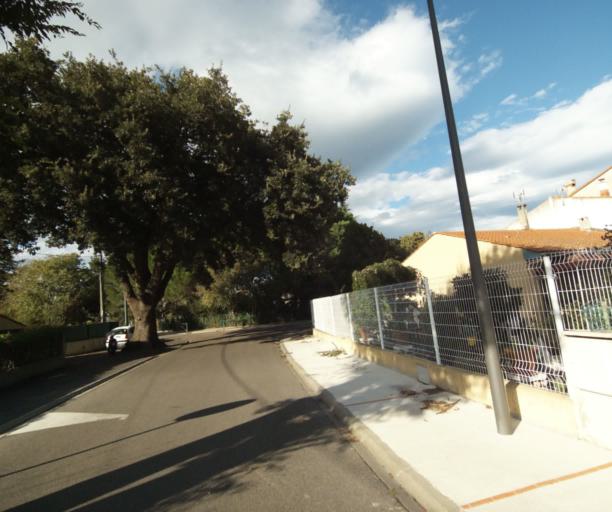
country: FR
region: Languedoc-Roussillon
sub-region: Departement des Pyrenees-Orientales
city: Argelers
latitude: 42.5448
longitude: 3.0309
